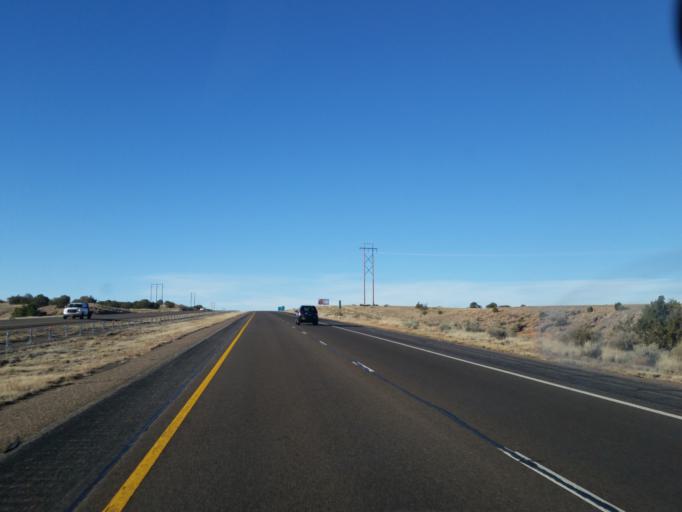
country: US
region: New Mexico
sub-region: Sandoval County
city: Santo Domingo Pueblo
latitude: 35.4818
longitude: -106.2768
